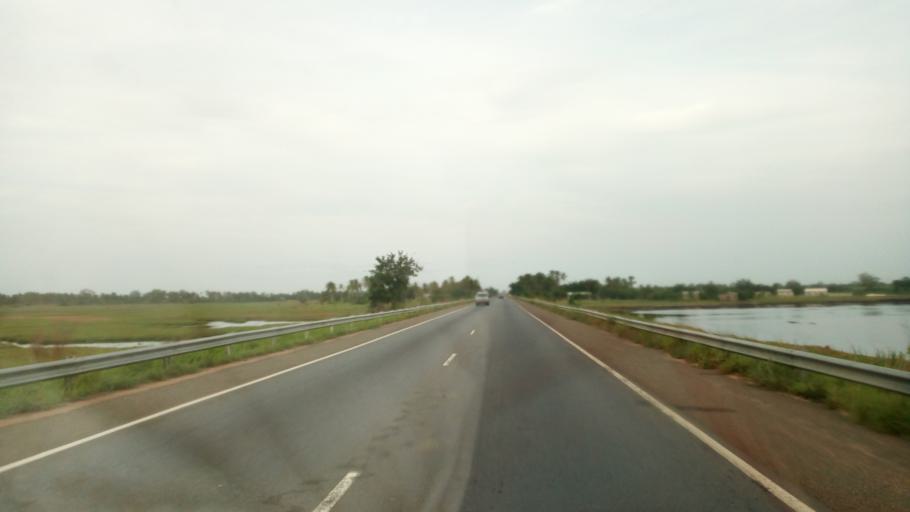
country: GH
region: Volta
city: Keta
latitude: 6.0694
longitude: 1.0225
